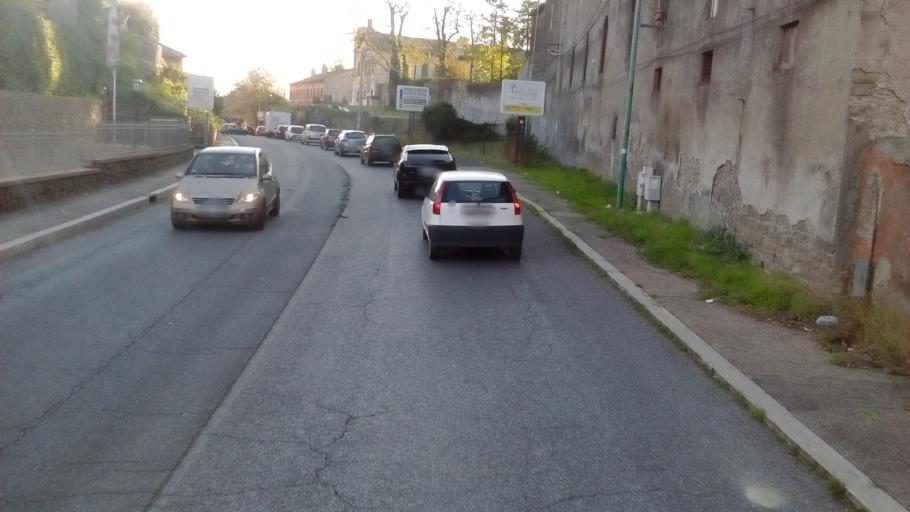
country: IT
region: Latium
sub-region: Citta metropolitana di Roma Capitale
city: Pavona
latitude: 41.7315
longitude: 12.6164
